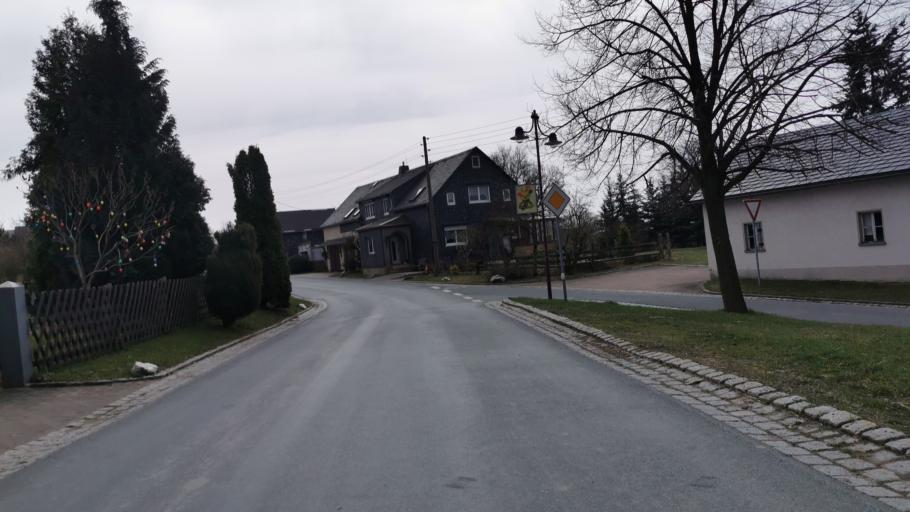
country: DE
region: Thuringia
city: Probstzella
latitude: 50.5373
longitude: 11.4243
